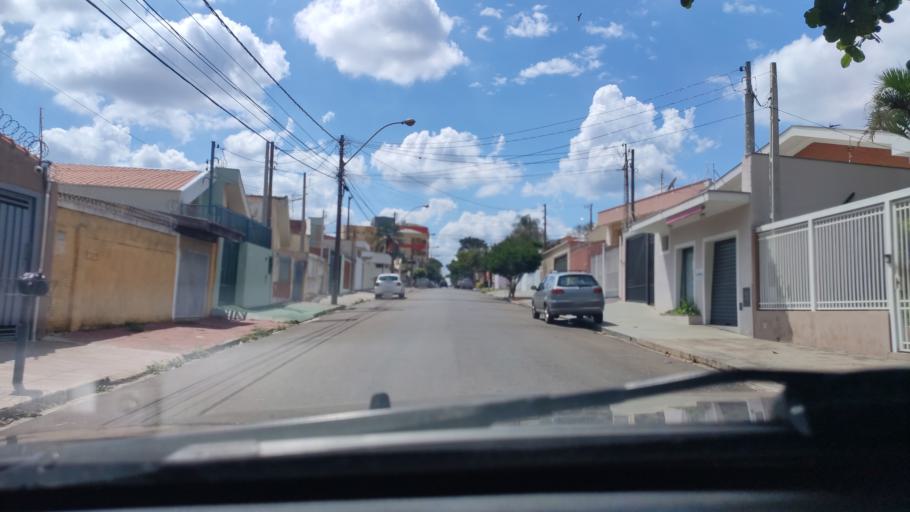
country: BR
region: Sao Paulo
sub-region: Sao Carlos
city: Sao Carlos
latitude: -22.0043
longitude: -47.8807
